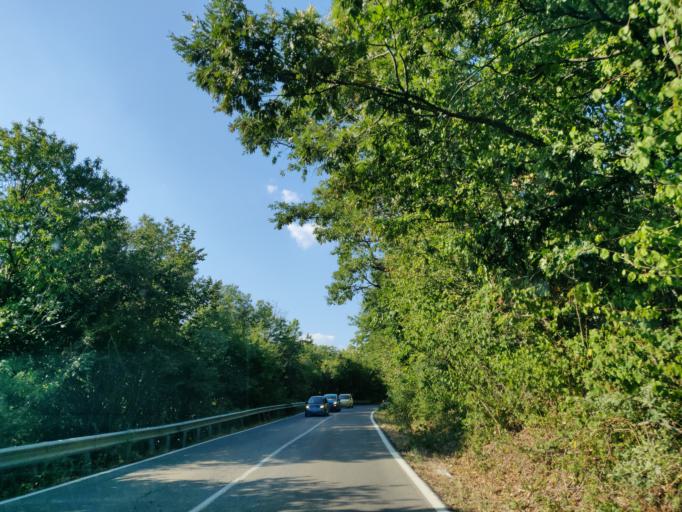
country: IT
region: Latium
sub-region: Provincia di Viterbo
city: Latera
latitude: 42.6161
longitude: 11.8394
